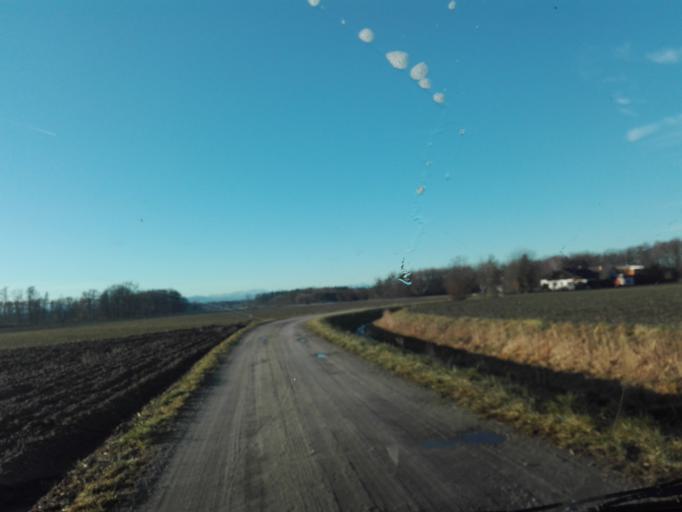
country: AT
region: Upper Austria
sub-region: Politischer Bezirk Perg
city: Perg
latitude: 48.2276
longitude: 14.6866
